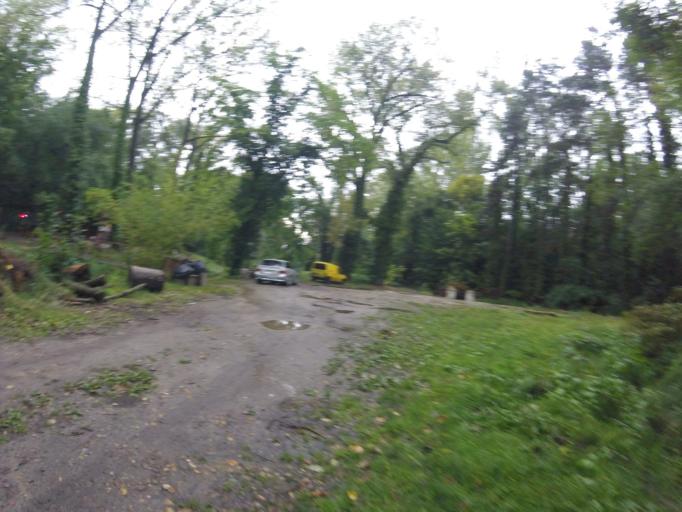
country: HU
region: Pest
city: God
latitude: 47.6729
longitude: 19.1260
